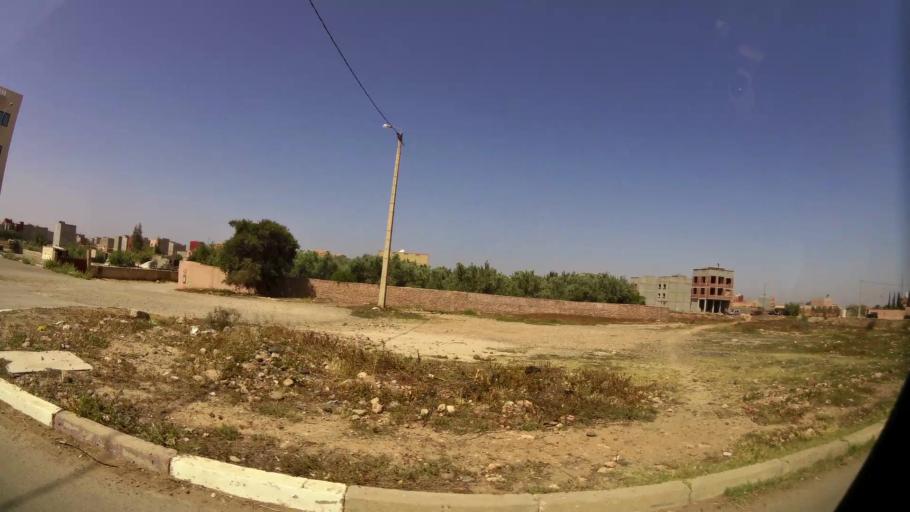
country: MA
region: Souss-Massa-Draa
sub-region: Inezgane-Ait Mellou
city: Inezgane
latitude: 30.3213
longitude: -9.5062
